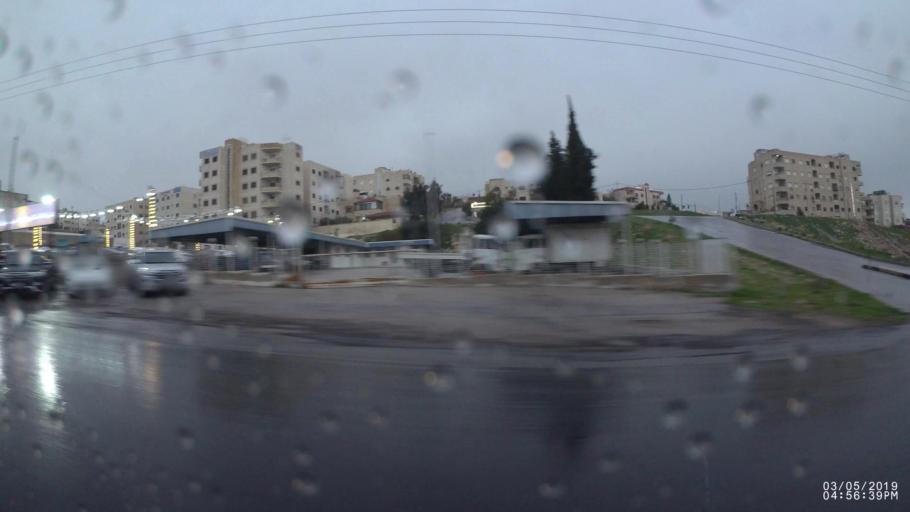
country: JO
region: Amman
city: Amman
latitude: 31.9869
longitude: 35.9662
